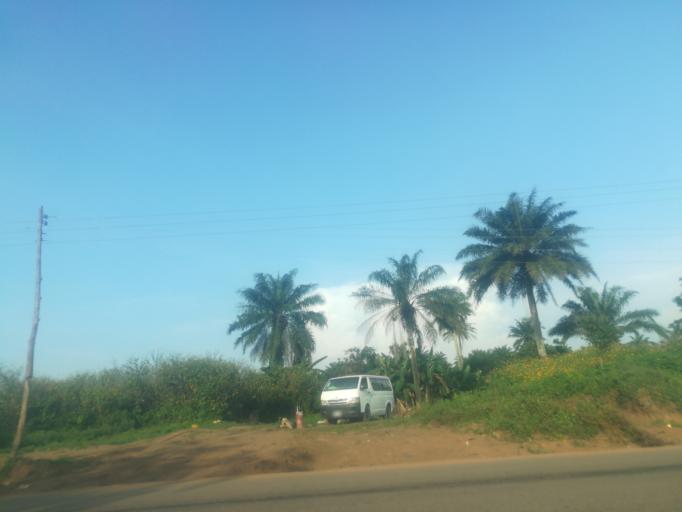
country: NG
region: Oyo
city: Moniya
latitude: 7.5500
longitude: 3.8919
